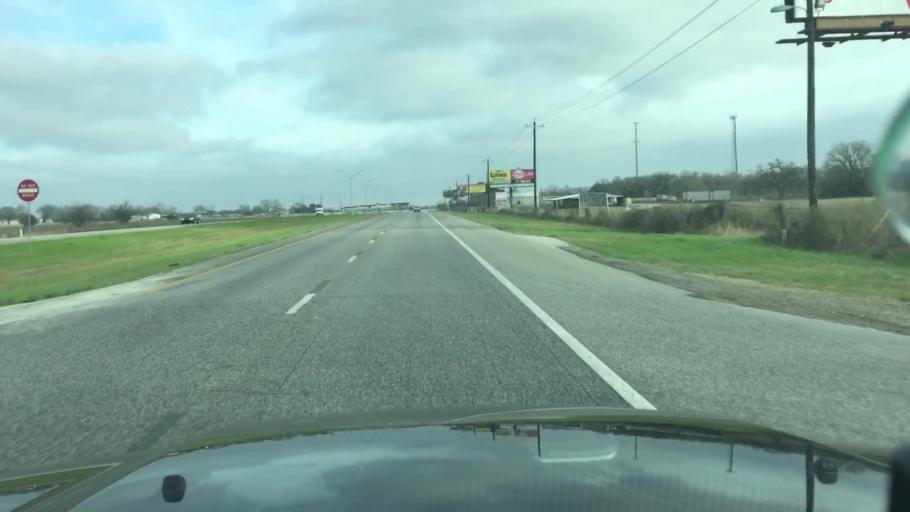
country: US
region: Texas
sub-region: Waller County
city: Hempstead
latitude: 30.1176
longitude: -96.0901
